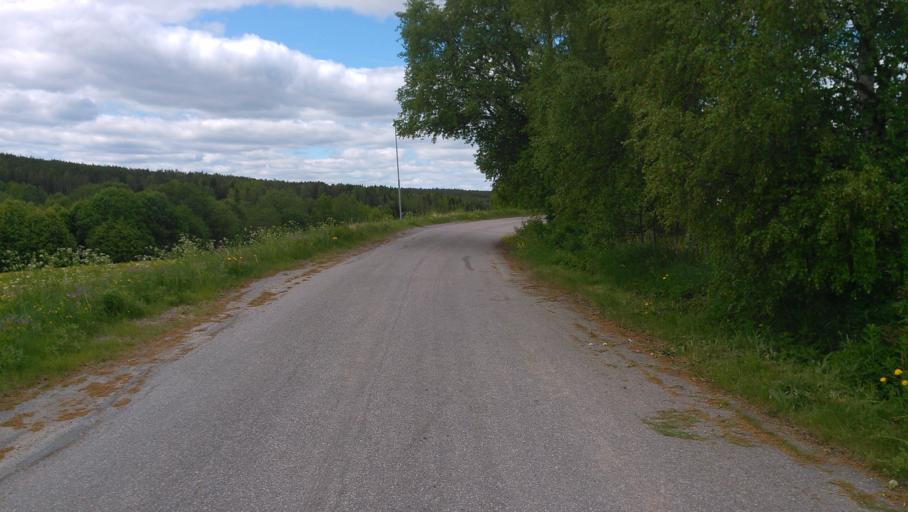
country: SE
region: Vaesterbotten
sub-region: Umea Kommun
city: Roback
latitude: 63.8579
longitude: 20.0921
